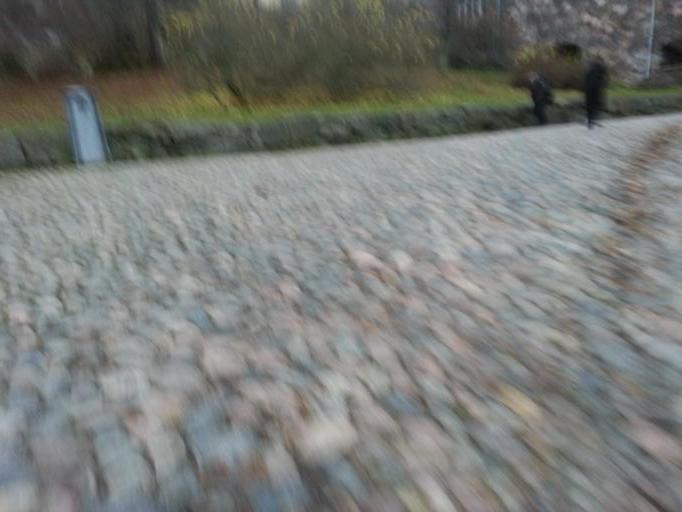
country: FI
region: Uusimaa
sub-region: Helsinki
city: Helsinki
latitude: 60.1443
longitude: 24.9866
